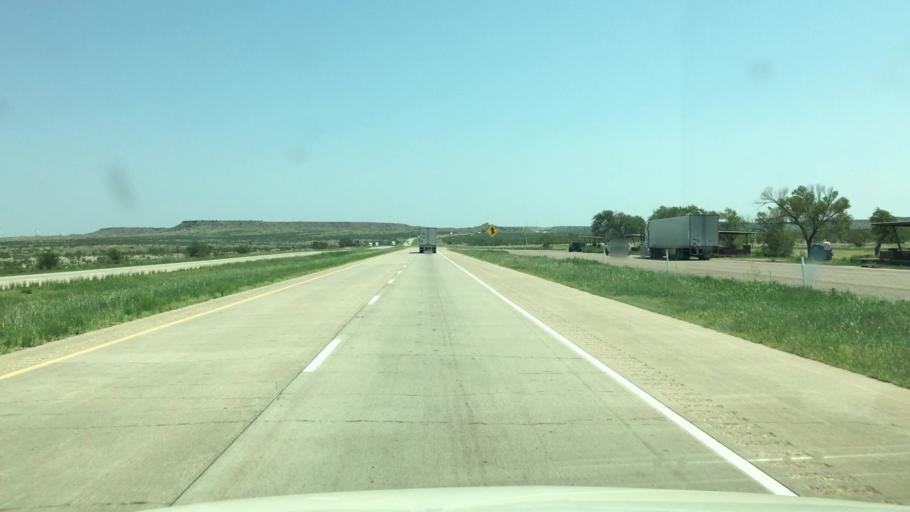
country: US
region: Texas
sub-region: Oldham County
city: Vega
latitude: 35.2375
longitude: -102.8356
